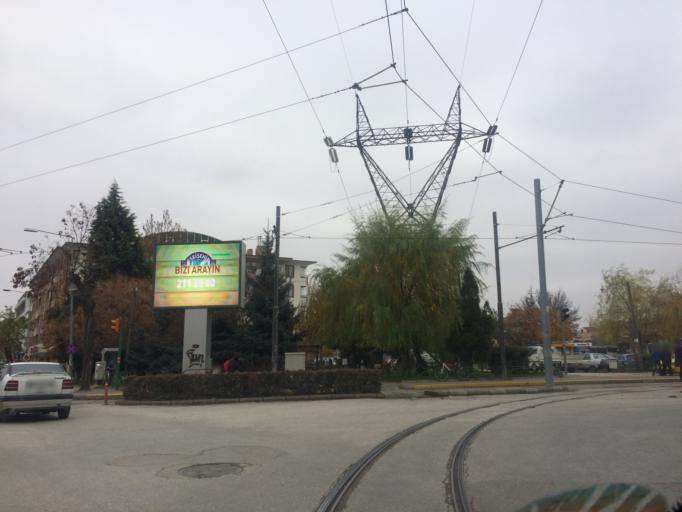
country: TR
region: Eskisehir
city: Eskisehir
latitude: 39.7900
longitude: 30.4850
